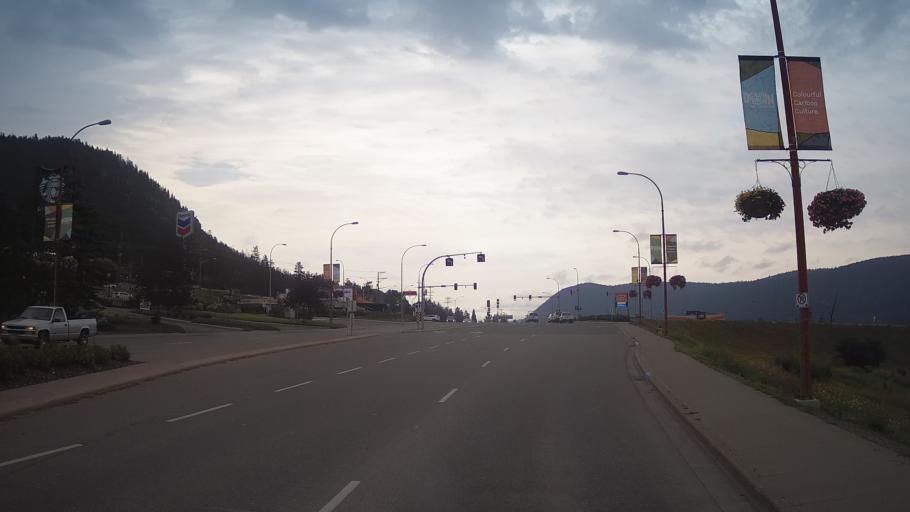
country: CA
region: British Columbia
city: Williams Lake
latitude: 52.1279
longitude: -122.1302
